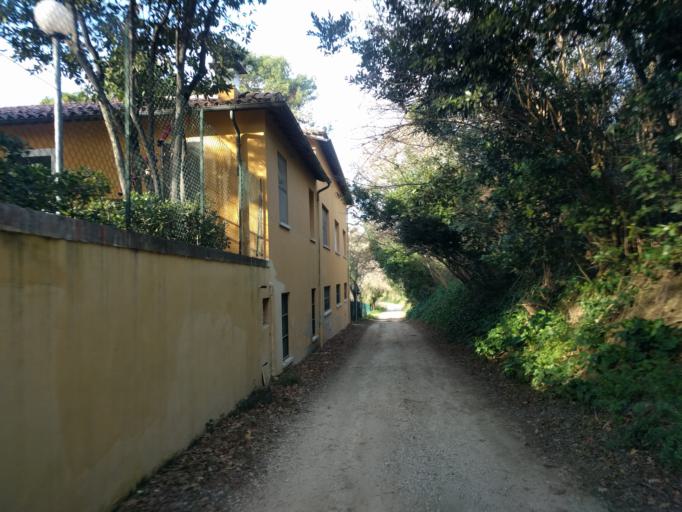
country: IT
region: The Marches
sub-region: Provincia di Pesaro e Urbino
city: Cuccurano
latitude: 43.8081
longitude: 12.9513
